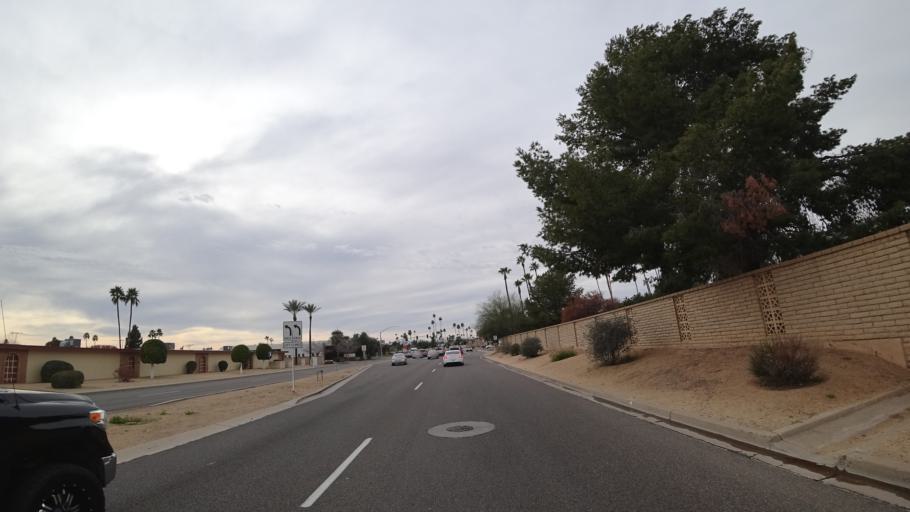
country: US
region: Arizona
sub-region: Maricopa County
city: Sun City
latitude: 33.6094
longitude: -112.2663
